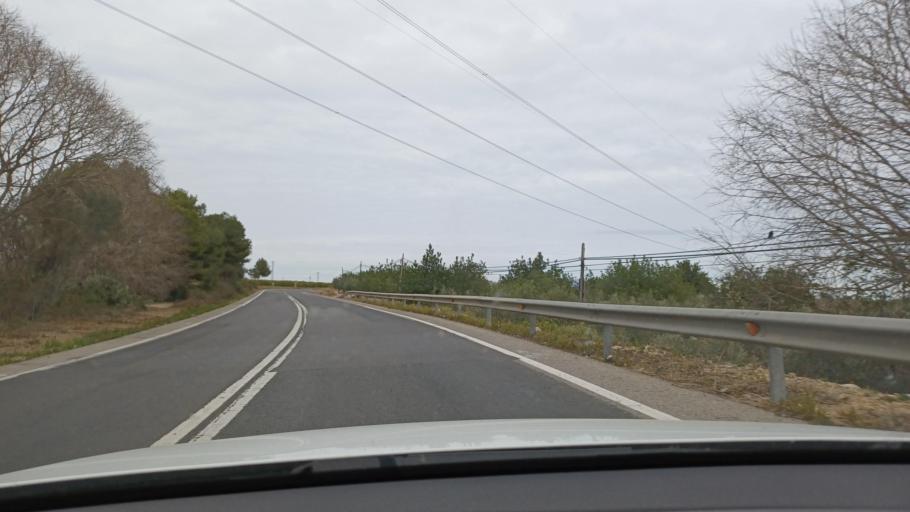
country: ES
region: Catalonia
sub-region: Provincia de Tarragona
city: Santa Barbara
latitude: 40.6916
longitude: 0.4747
